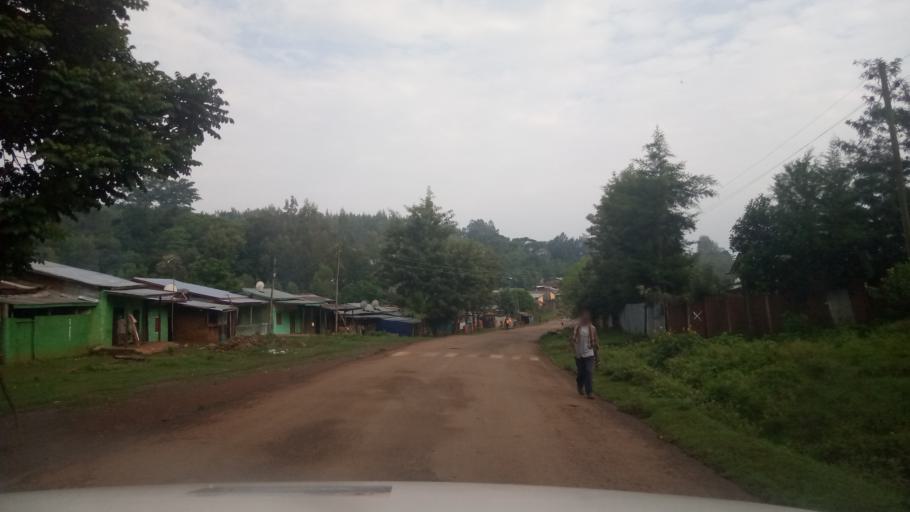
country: ET
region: Oromiya
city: Agaro
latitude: 7.8383
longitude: 36.6659
